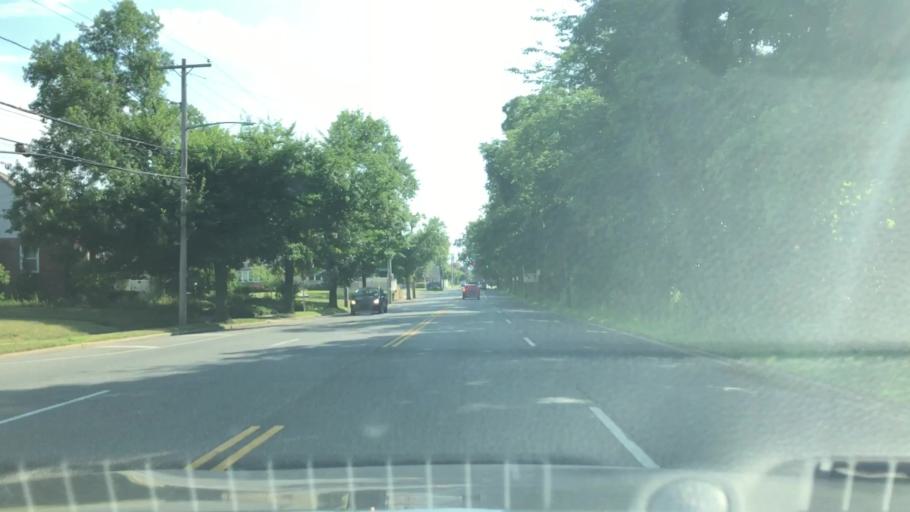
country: US
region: New York
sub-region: Nassau County
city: North Valley Stream
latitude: 40.6791
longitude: -73.6907
